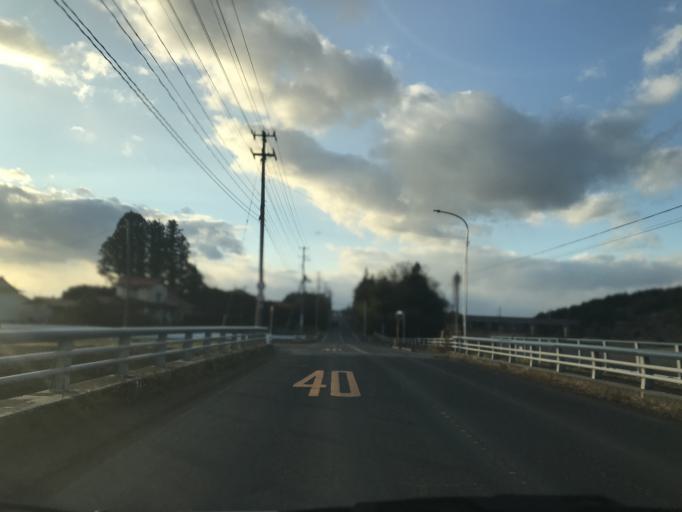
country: JP
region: Miyagi
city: Kogota
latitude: 38.6573
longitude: 141.0270
